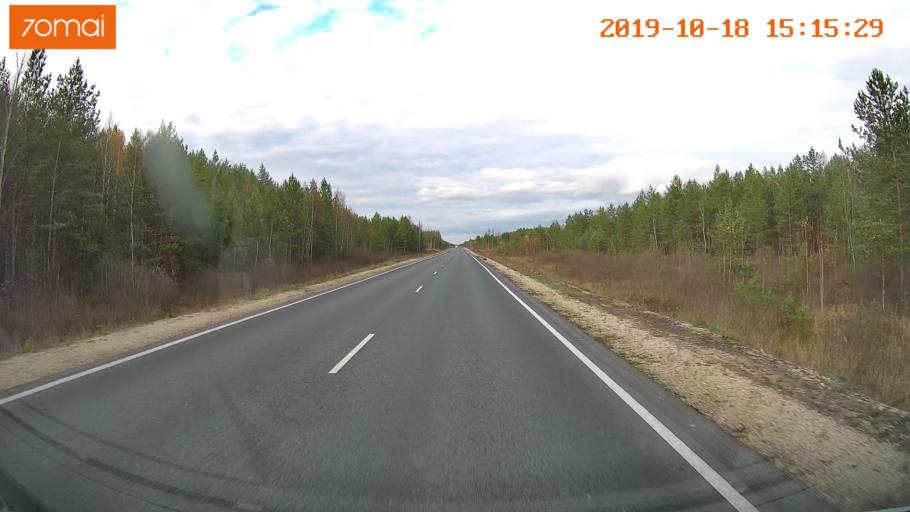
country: RU
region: Vladimir
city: Gus'-Khrustal'nyy
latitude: 55.6196
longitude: 40.7226
